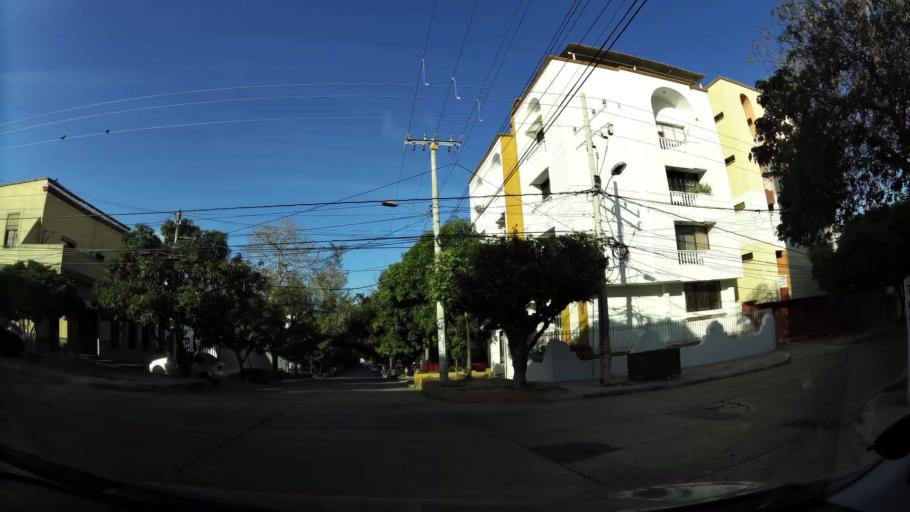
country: CO
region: Atlantico
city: Barranquilla
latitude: 10.9884
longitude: -74.8069
